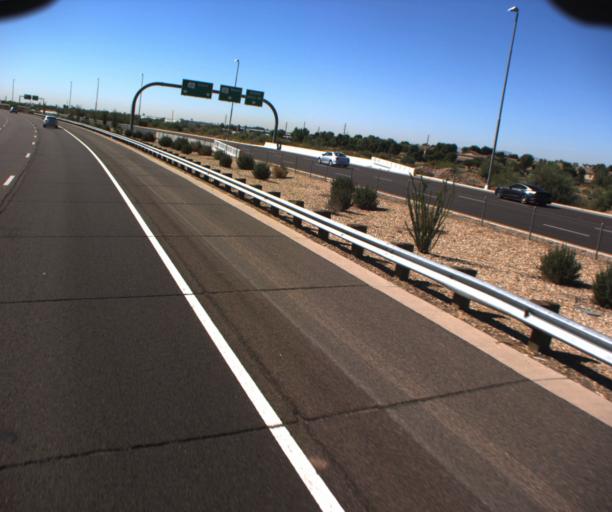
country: US
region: Arizona
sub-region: Maricopa County
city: Sun City
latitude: 33.6633
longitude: -112.2308
